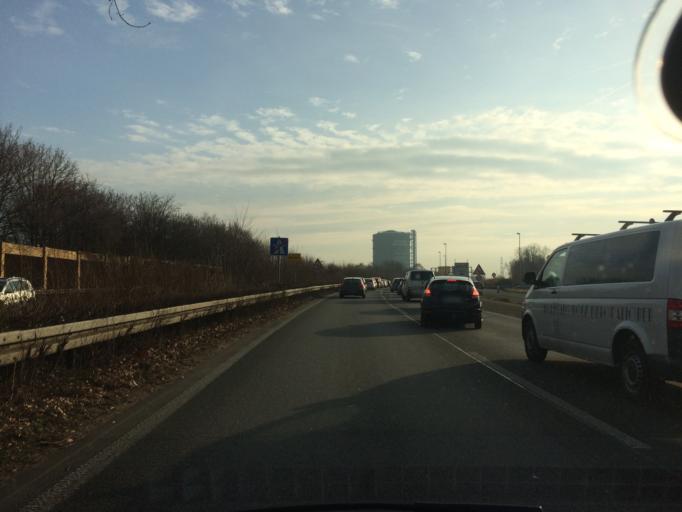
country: DE
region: North Rhine-Westphalia
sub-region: Regierungsbezirk Dusseldorf
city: Oberhausen
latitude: 51.5024
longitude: 6.8624
